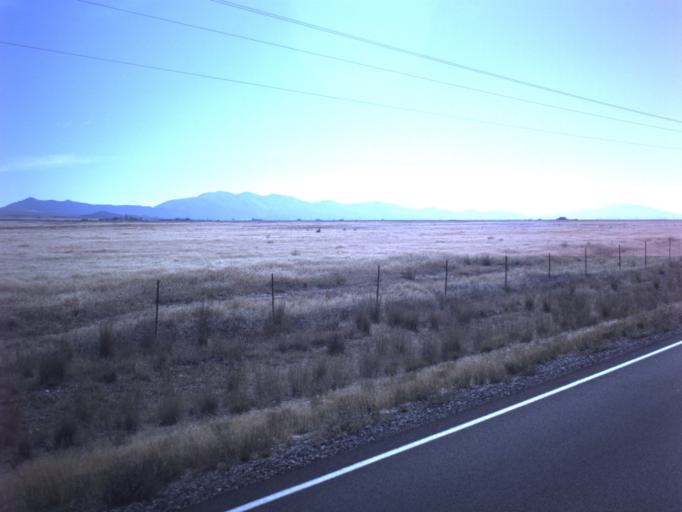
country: US
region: Utah
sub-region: Tooele County
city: Grantsville
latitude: 40.4184
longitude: -112.7488
